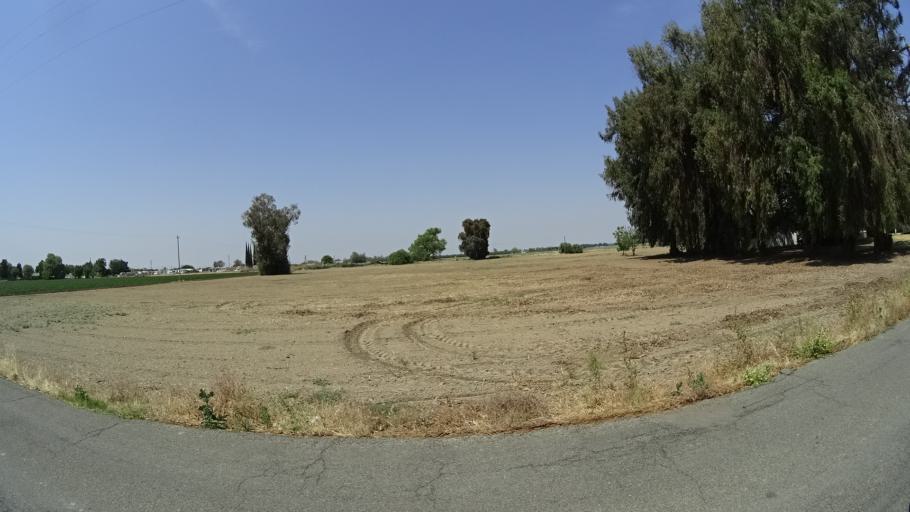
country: US
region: California
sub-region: Kings County
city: Lemoore
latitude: 36.3175
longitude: -119.7943
